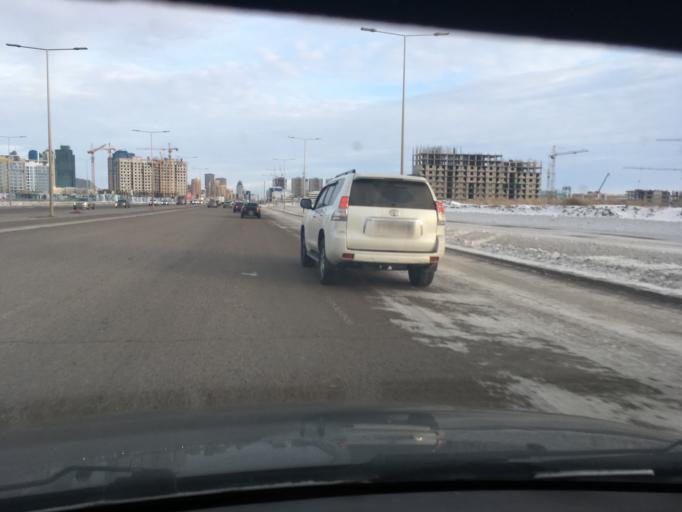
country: KZ
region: Astana Qalasy
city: Astana
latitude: 51.1289
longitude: 71.3891
